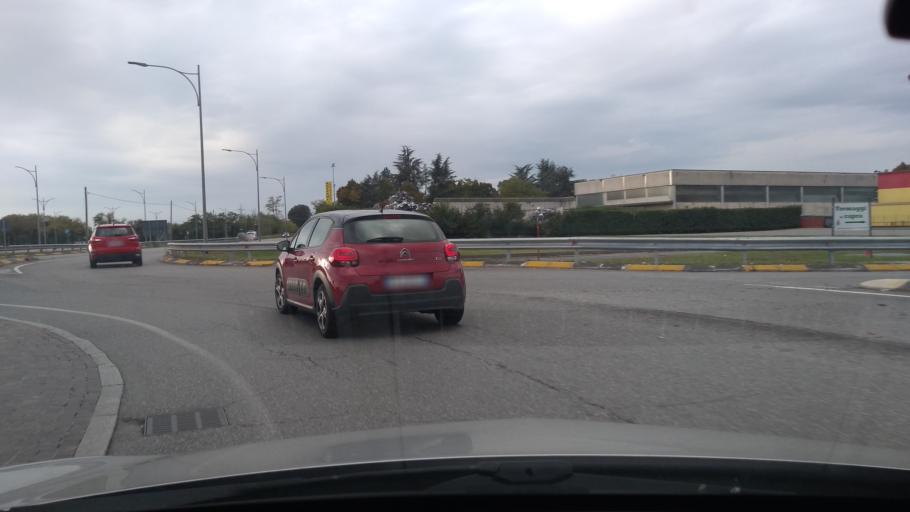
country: IT
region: Lombardy
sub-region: Provincia di Bergamo
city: Cologno al Serio
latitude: 45.5890
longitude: 9.7163
